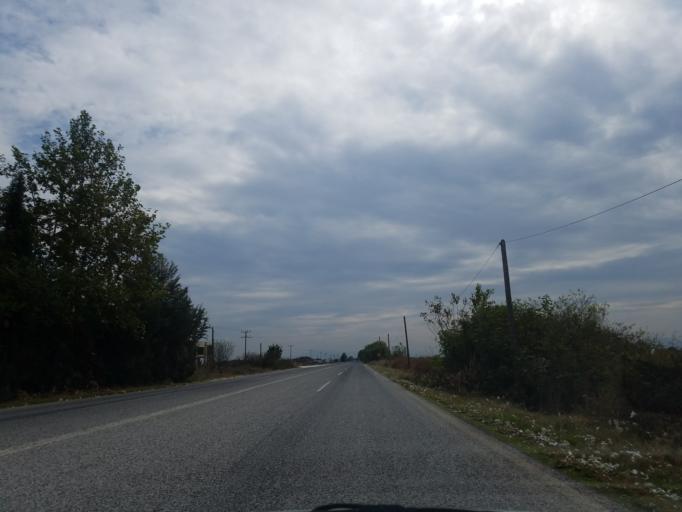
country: GR
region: Thessaly
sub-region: Nomos Kardhitsas
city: Karpochori
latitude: 39.3660
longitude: 22.0290
